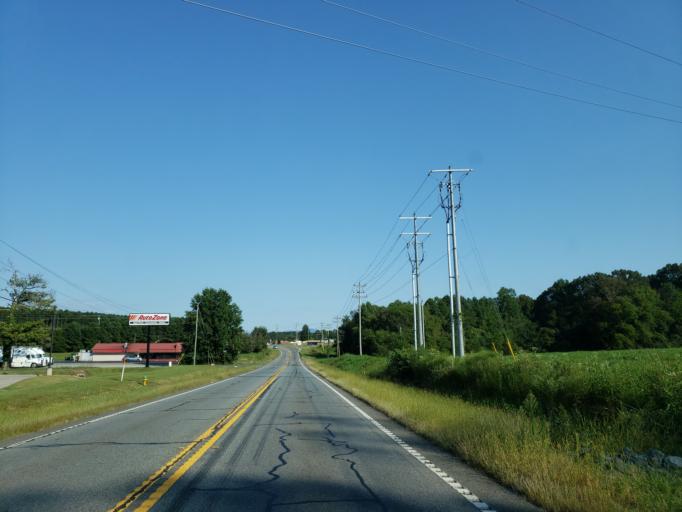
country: US
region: Georgia
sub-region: Whitfield County
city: Varnell
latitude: 34.8962
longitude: -84.9515
